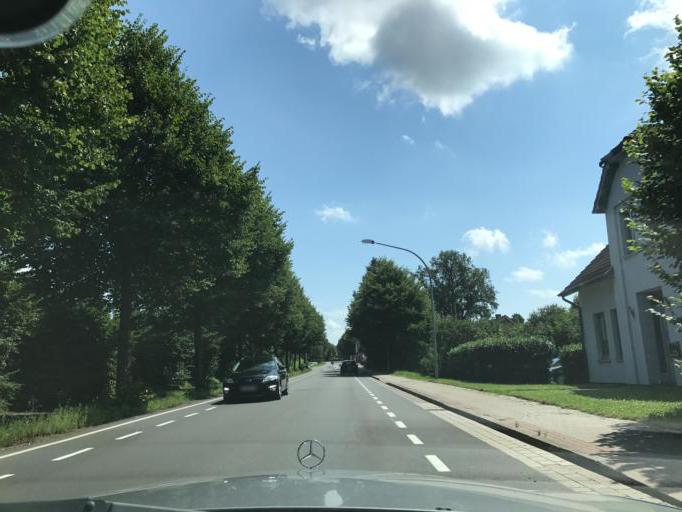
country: DE
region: Lower Saxony
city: Hagen
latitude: 52.1981
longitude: 7.9444
